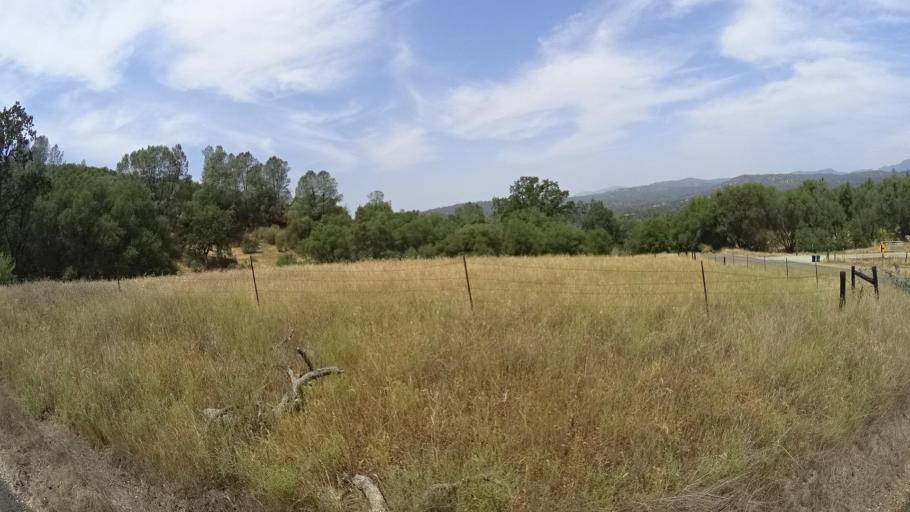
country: US
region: California
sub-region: Madera County
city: Ahwahnee
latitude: 37.4068
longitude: -119.8494
